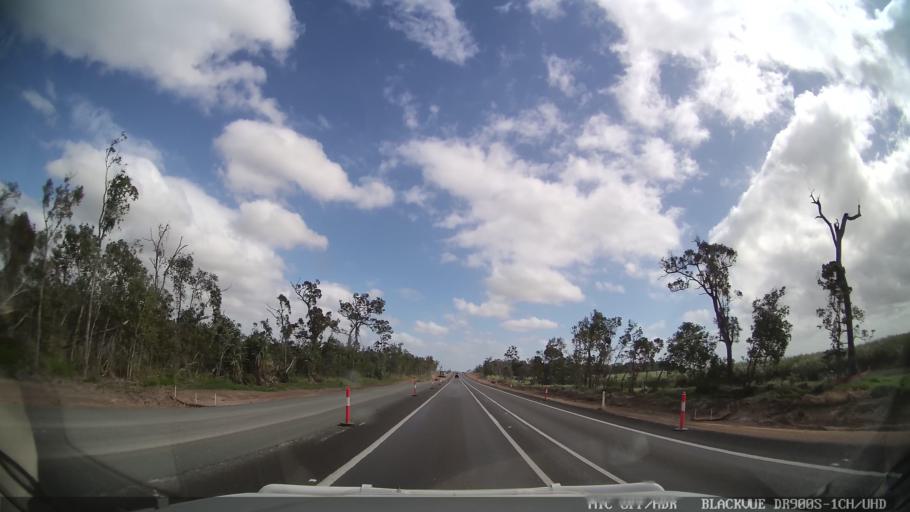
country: AU
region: Queensland
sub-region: Whitsunday
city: Red Hill
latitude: -20.2972
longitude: 148.5063
